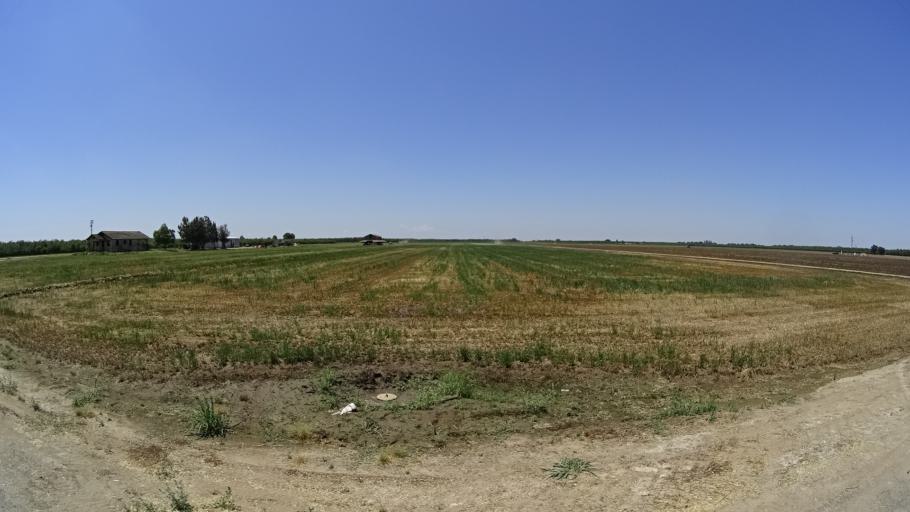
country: US
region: California
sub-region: Kings County
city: Lucerne
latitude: 36.4064
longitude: -119.6010
